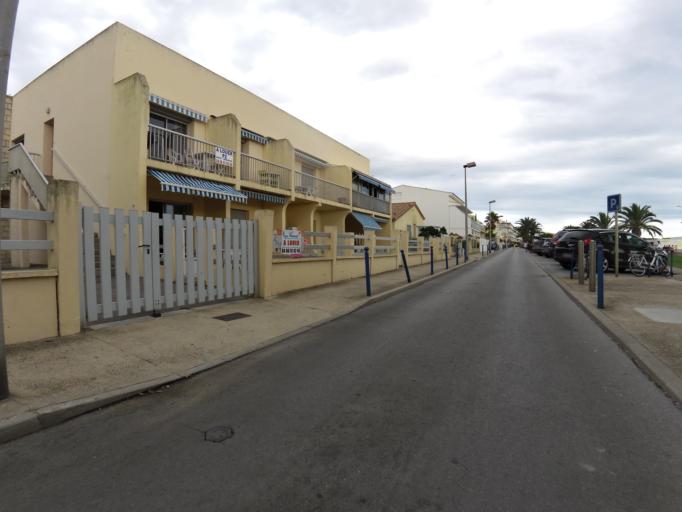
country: FR
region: Languedoc-Roussillon
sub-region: Departement du Gard
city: Le Grau-du-Roi
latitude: 43.5330
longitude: 4.1388
